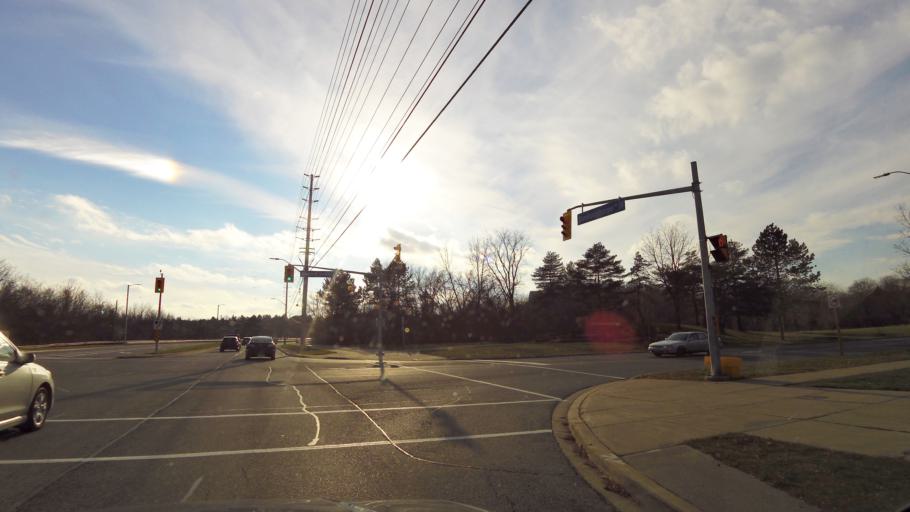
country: CA
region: Ontario
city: Mississauga
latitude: 43.5507
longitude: -79.6768
